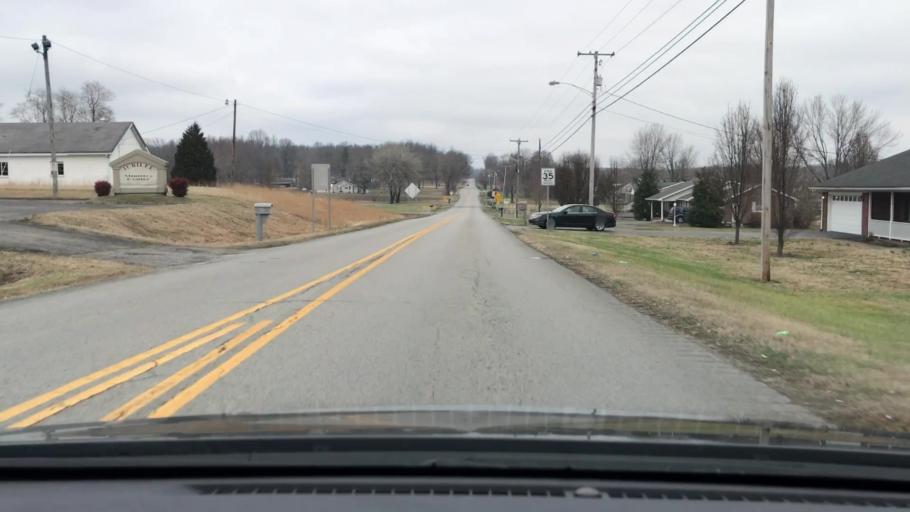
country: US
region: Kentucky
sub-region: Muhlenberg County
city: Greenville
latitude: 37.2200
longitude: -87.1939
